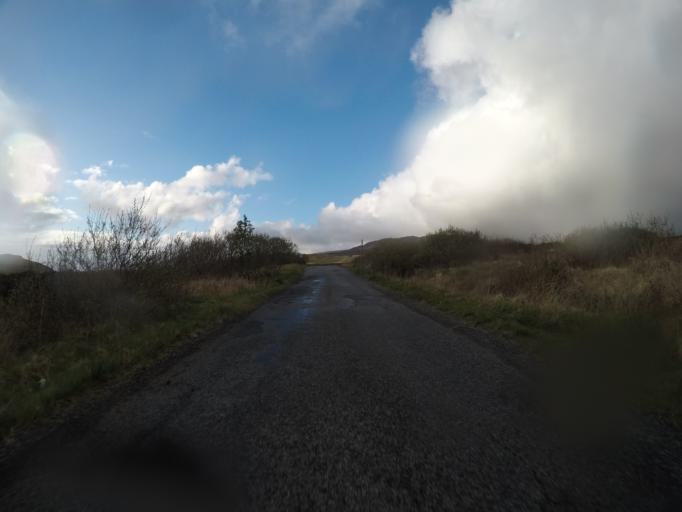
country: GB
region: Scotland
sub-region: Highland
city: Portree
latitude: 57.4731
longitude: -6.2980
